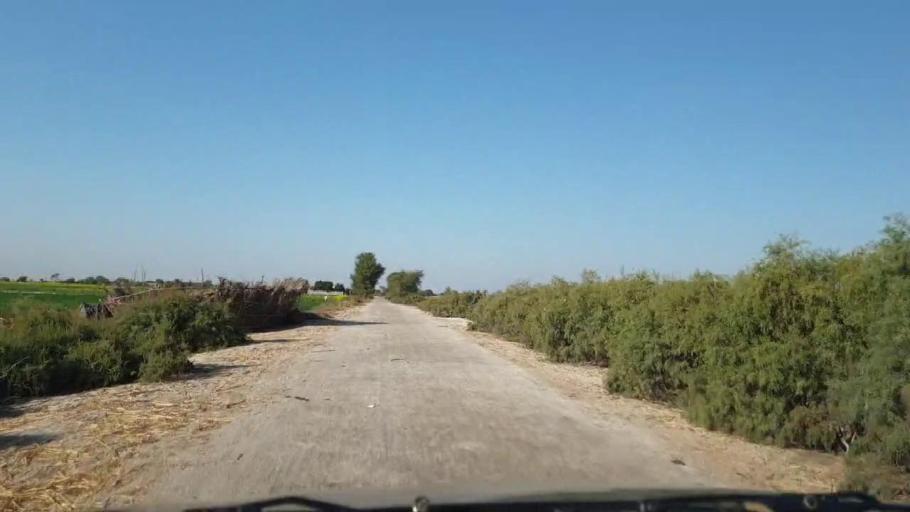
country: PK
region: Sindh
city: Khadro
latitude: 26.2082
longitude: 68.7543
